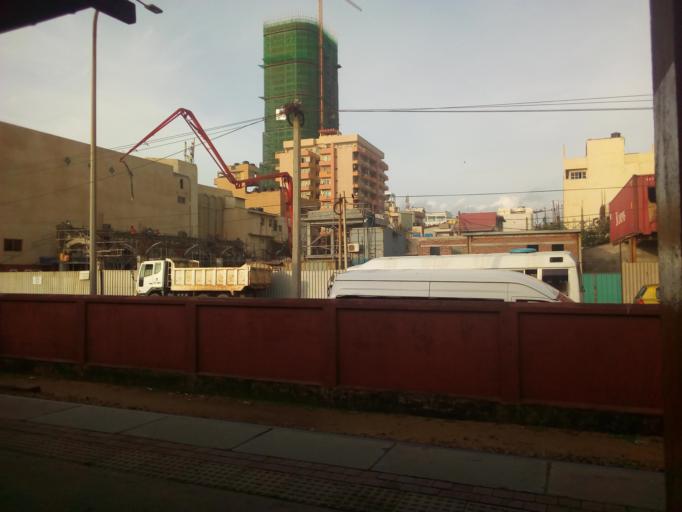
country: LK
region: Western
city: Colombo
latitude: 6.8937
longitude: 79.8530
